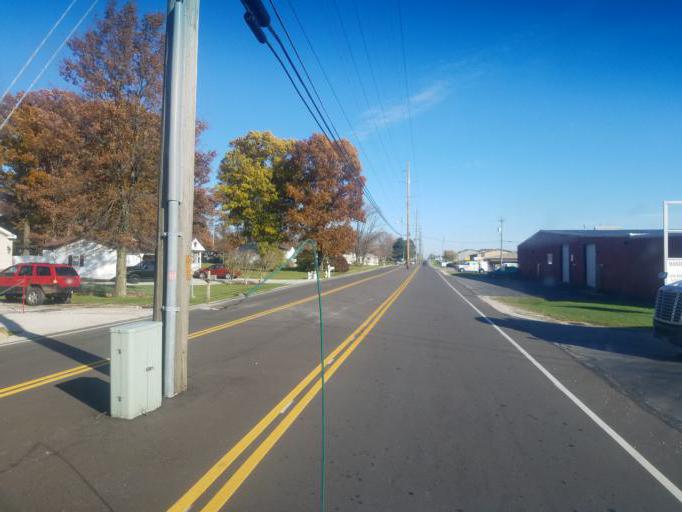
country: US
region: Ohio
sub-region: Richland County
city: Ontario
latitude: 40.7762
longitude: -82.5591
